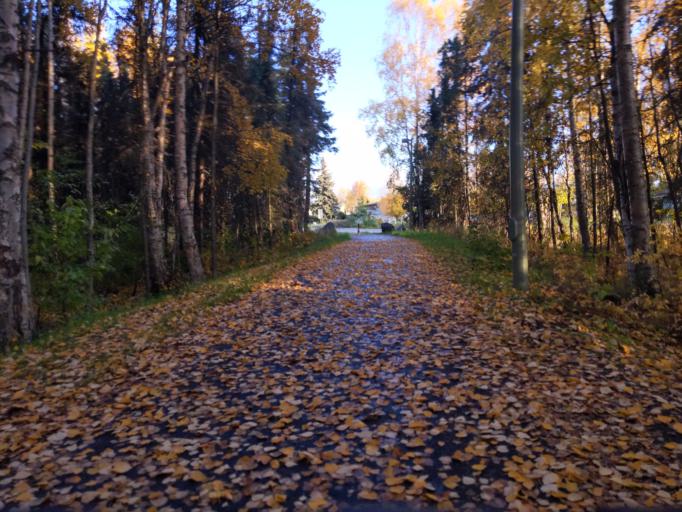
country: US
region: Alaska
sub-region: Anchorage Municipality
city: Anchorage
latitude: 61.1559
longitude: -149.8732
